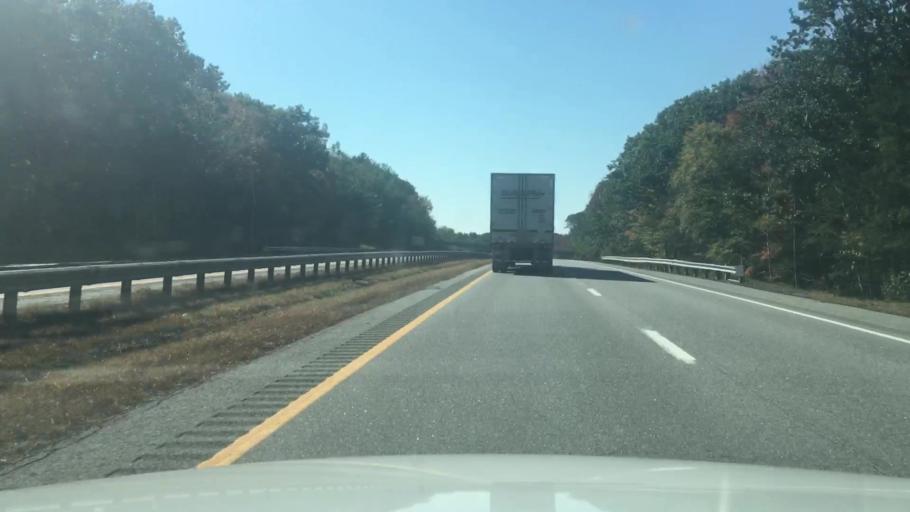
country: US
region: Maine
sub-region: Cumberland County
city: Falmouth
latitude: 43.7265
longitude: -70.2900
